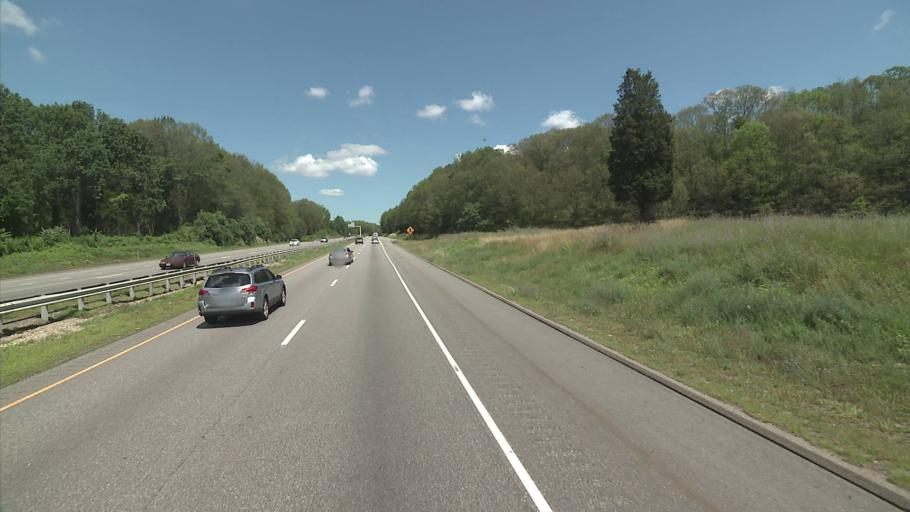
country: US
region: Connecticut
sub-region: New London County
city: Oxoboxo River
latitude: 41.4426
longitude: -72.1173
